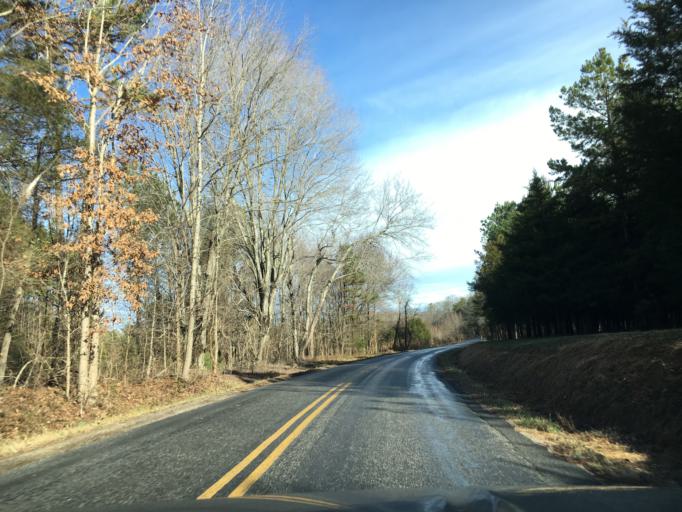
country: US
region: Virginia
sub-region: Cumberland County
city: Cumberland
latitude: 37.3471
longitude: -78.1584
